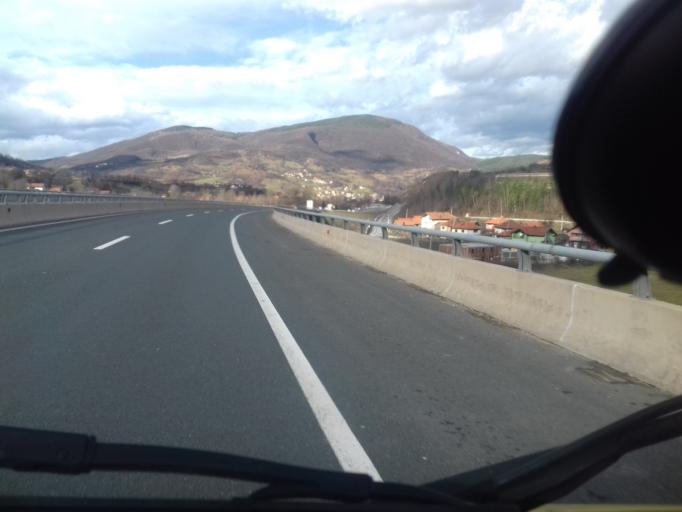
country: BA
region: Federation of Bosnia and Herzegovina
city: Kakanj
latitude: 44.1256
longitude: 18.0922
